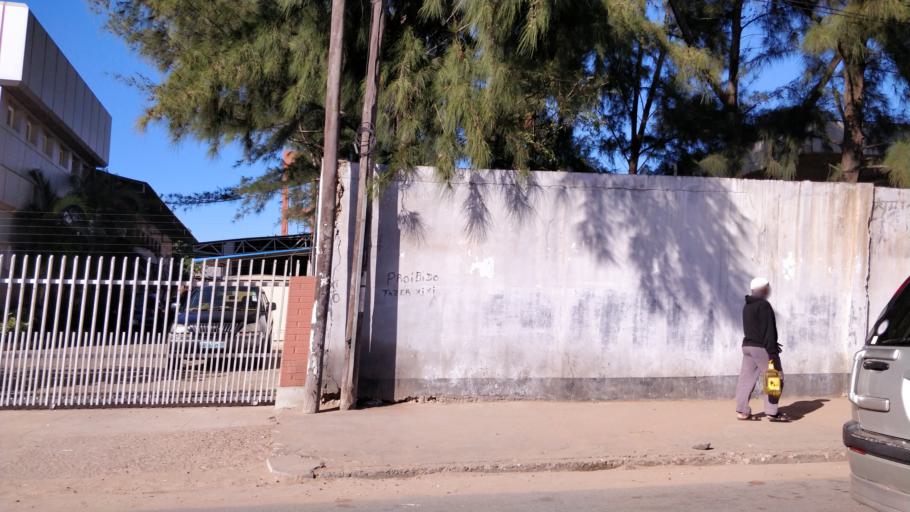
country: MZ
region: Maputo City
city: Maputo
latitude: -25.9273
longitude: 32.6037
